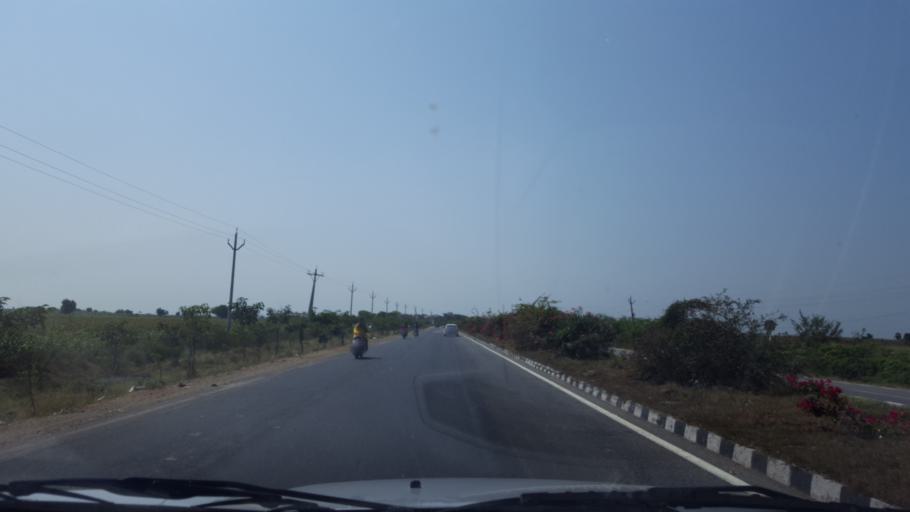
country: IN
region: Andhra Pradesh
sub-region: Guntur
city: Chilakalurupet
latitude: 16.0585
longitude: 80.1478
